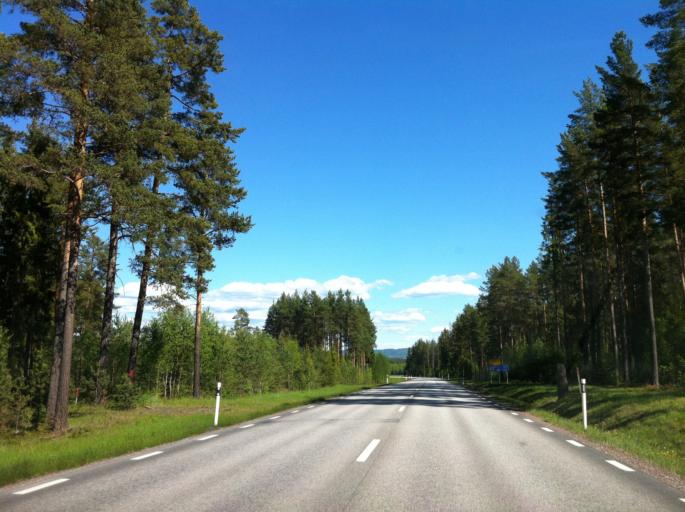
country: SE
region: Dalarna
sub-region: Rattviks Kommun
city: Vikarbyn
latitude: 60.9060
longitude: 14.9386
